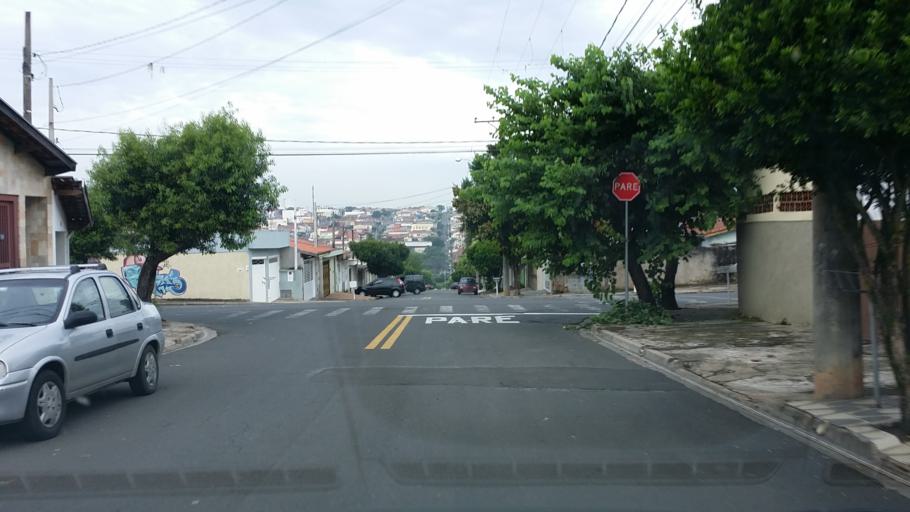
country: BR
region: Sao Paulo
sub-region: Indaiatuba
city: Indaiatuba
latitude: -23.1171
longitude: -47.2280
